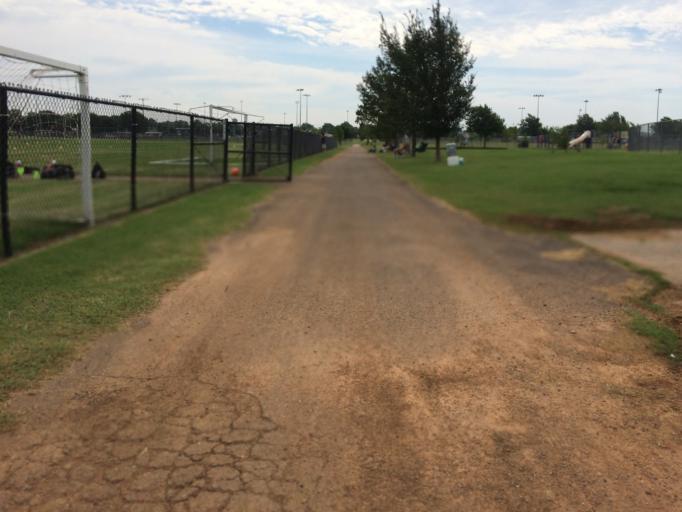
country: US
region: Oklahoma
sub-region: Cleveland County
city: Norman
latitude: 35.2348
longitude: -97.4283
